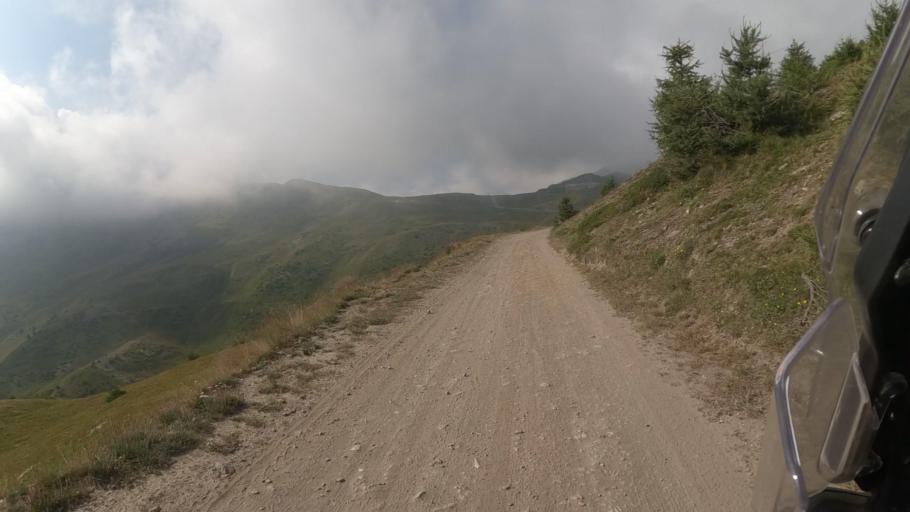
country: IT
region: Piedmont
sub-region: Provincia di Torino
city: Sestriere
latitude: 44.9914
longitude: 6.8713
